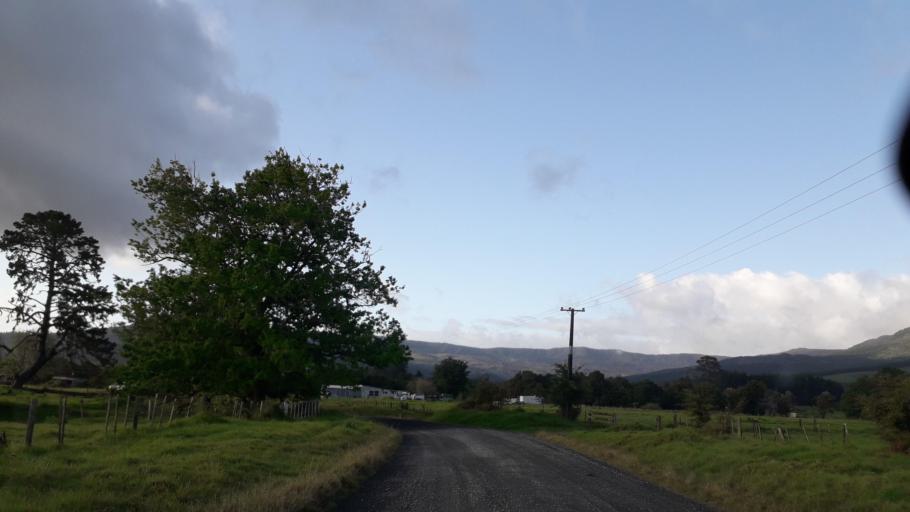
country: NZ
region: Northland
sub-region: Far North District
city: Waimate North
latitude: -35.5005
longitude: 173.6986
